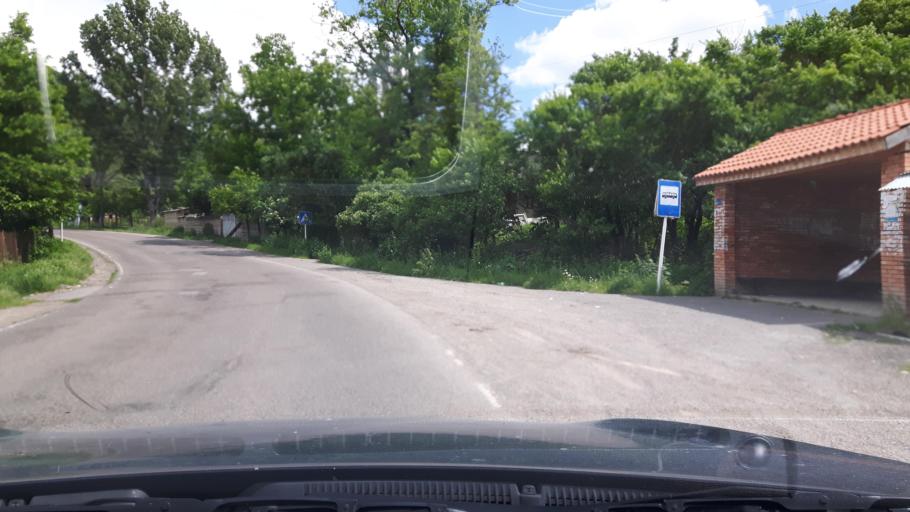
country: GE
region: Kakheti
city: Sagarejo
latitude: 41.8573
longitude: 45.2143
